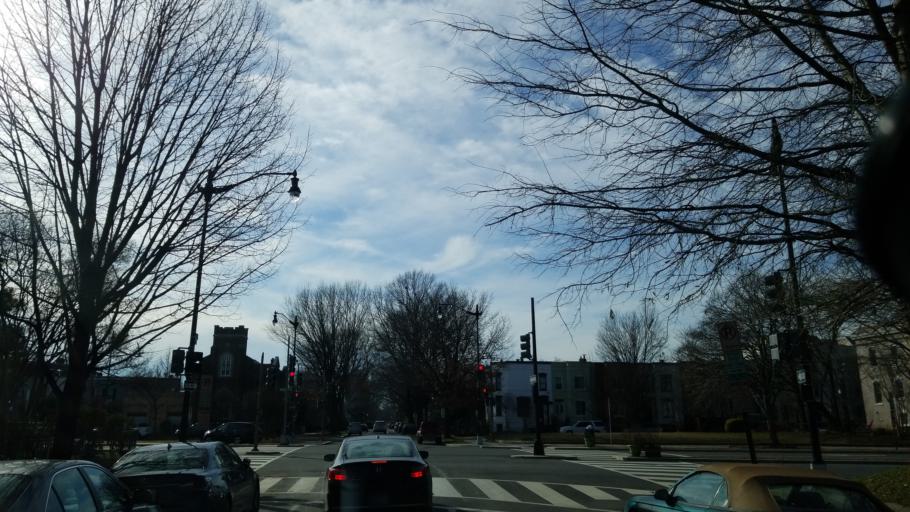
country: US
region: Washington, D.C.
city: Washington, D.C.
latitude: 38.8883
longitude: -76.9855
